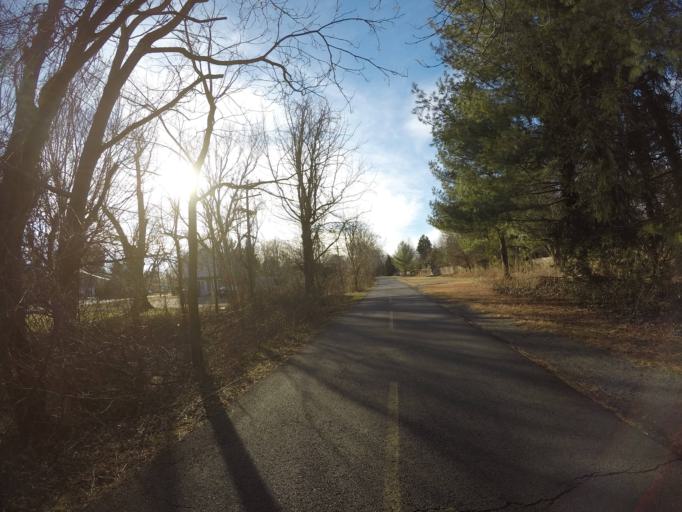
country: US
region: Virginia
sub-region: Loudoun County
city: Leesburg
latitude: 39.1133
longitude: -77.5752
